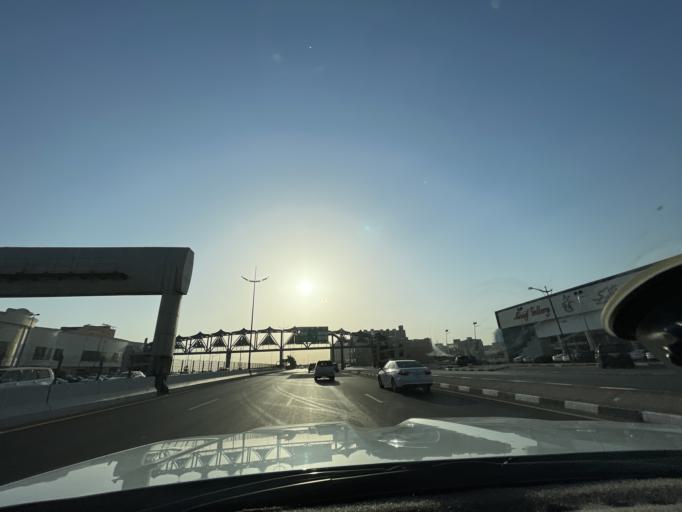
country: SA
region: Eastern Province
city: Khobar
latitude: 26.2876
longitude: 50.1854
